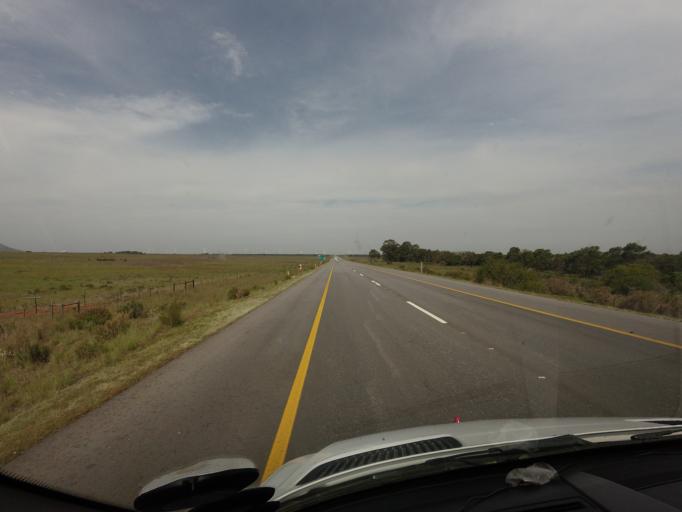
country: ZA
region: Eastern Cape
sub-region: Cacadu District Municipality
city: Kruisfontein
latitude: -34.0016
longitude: 24.7617
